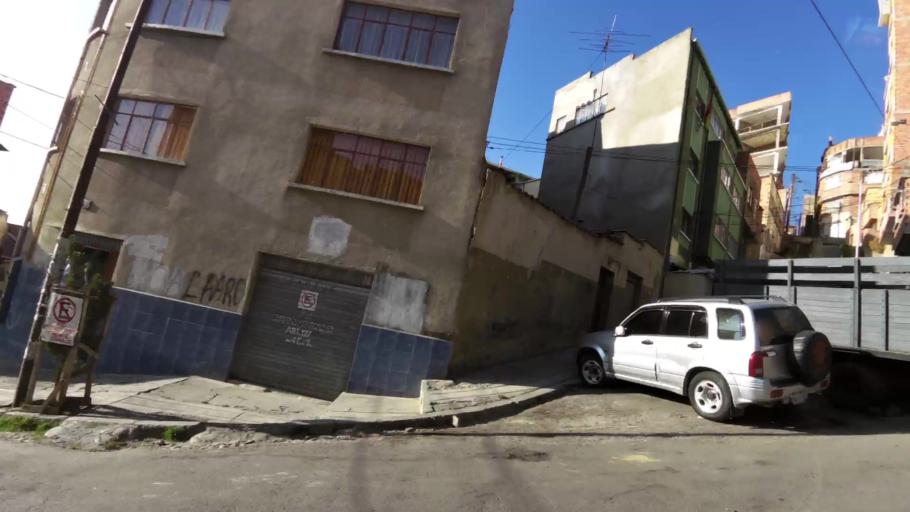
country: BO
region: La Paz
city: La Paz
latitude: -16.5035
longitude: -68.1428
